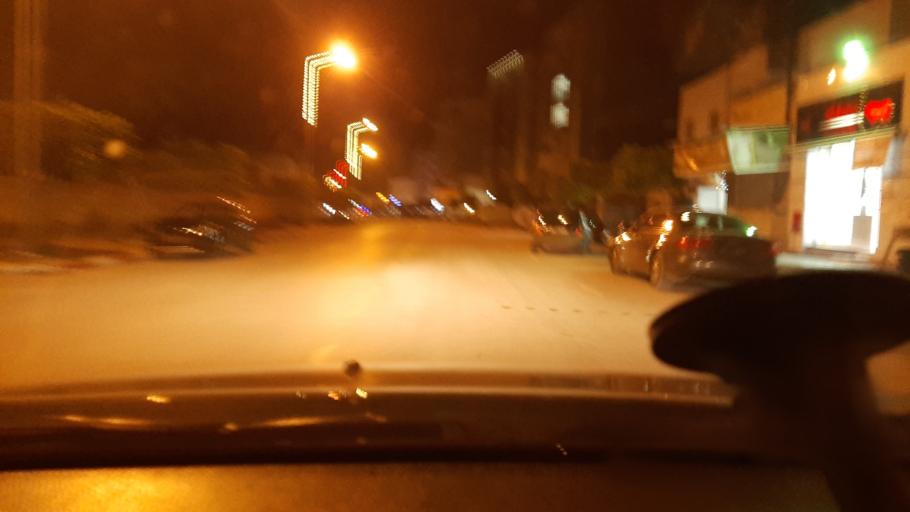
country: TN
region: Safaqis
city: Sfax
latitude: 34.7822
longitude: 10.7230
